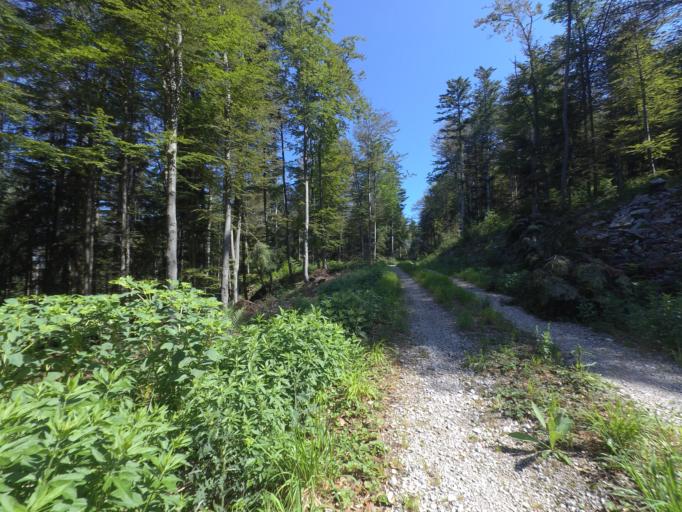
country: AT
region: Salzburg
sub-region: Politischer Bezirk Salzburg-Umgebung
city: Elsbethen
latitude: 47.7473
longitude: 13.1217
